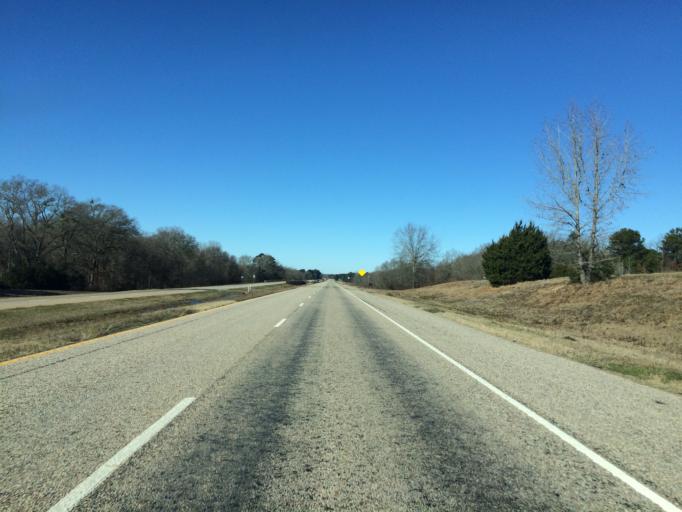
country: US
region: Texas
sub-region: Smith County
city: Lindale
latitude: 32.6278
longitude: -95.3382
